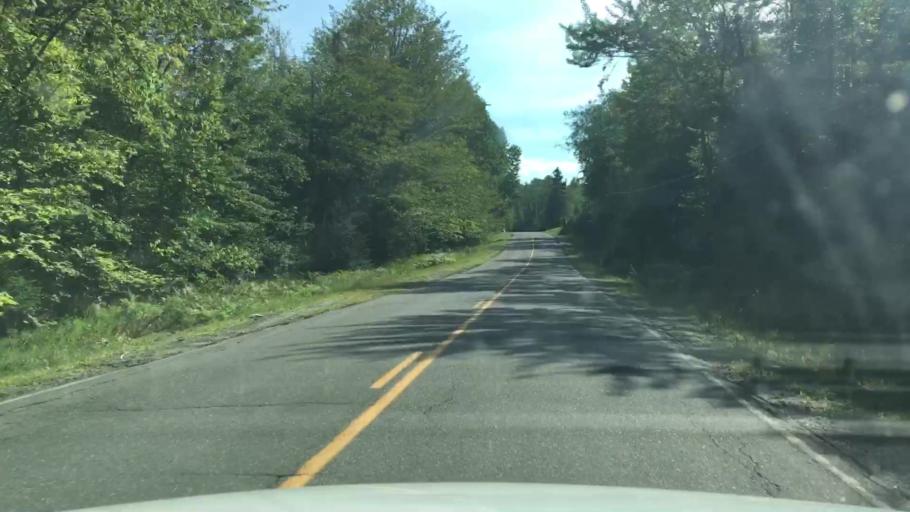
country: US
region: Maine
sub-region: Penobscot County
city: Enfield
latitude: 45.2949
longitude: -68.5552
